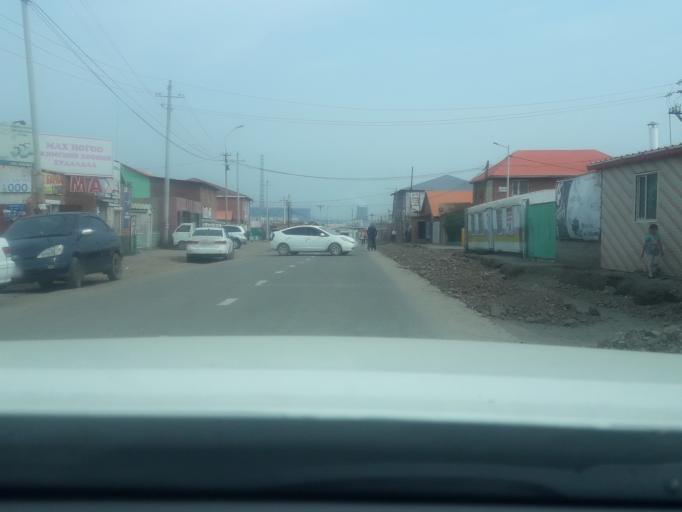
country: MN
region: Ulaanbaatar
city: Ulaanbaatar
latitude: 47.8710
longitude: 106.8066
